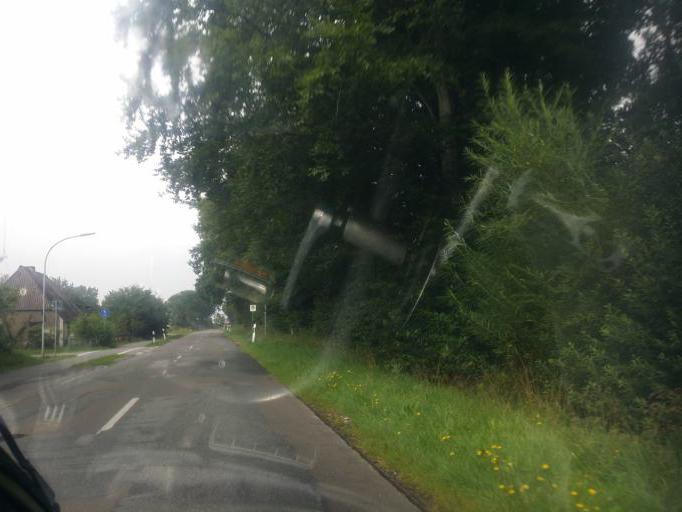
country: DE
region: Schleswig-Holstein
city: Hennstedt
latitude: 54.2678
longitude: 9.1571
